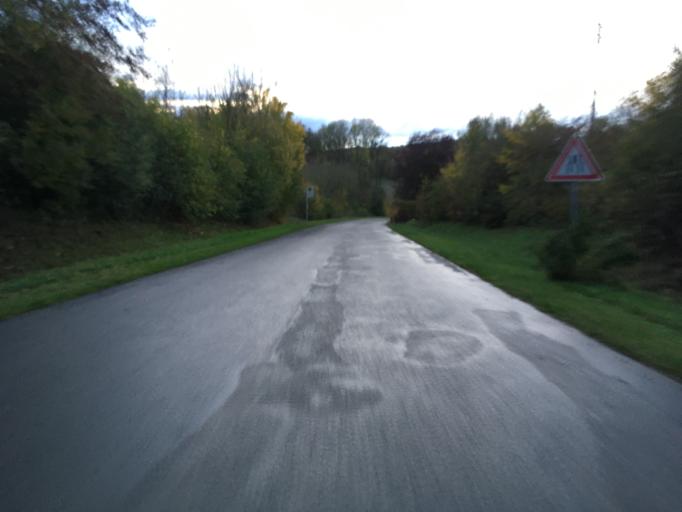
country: DE
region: Baden-Wuerttemberg
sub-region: Karlsruhe Region
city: Osterburken
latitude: 49.3918
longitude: 9.4678
